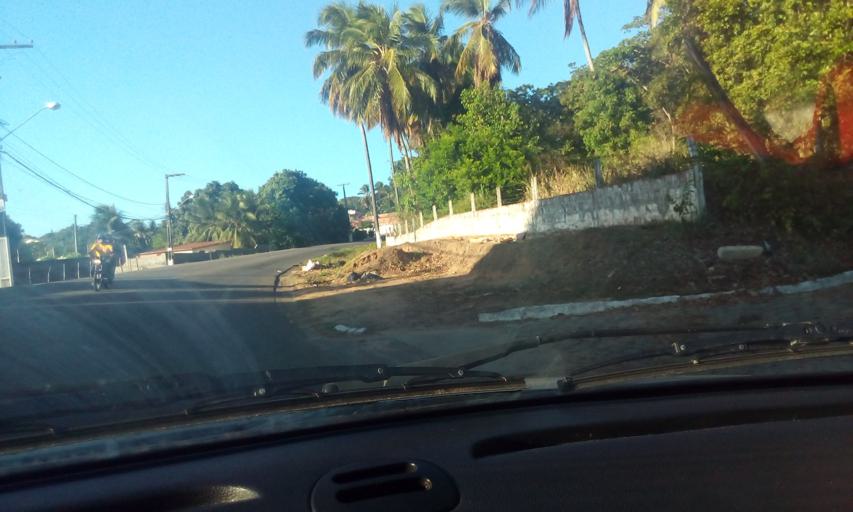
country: BR
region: Rio Grande do Norte
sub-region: Parnamirim
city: Parnamirim
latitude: -5.9525
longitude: -35.1626
